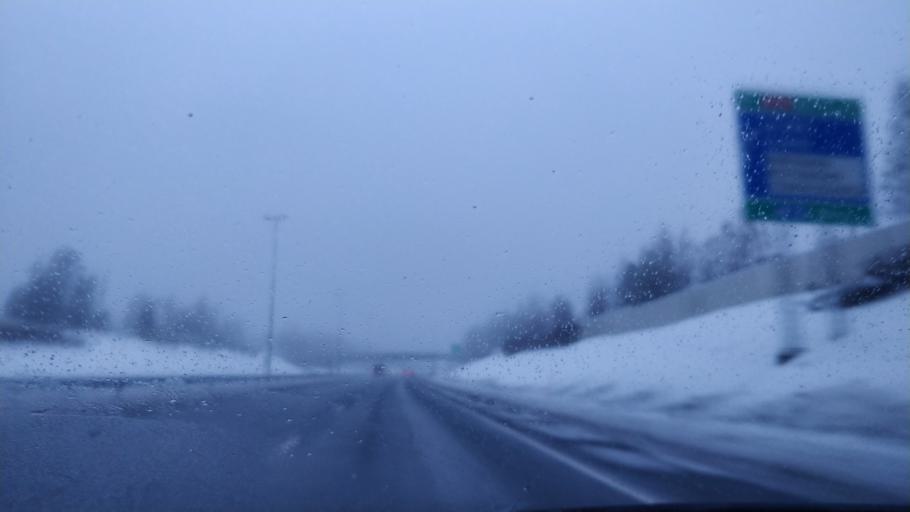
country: FI
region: Lapland
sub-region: Kemi-Tornio
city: Kemi
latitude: 65.7487
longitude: 24.5773
